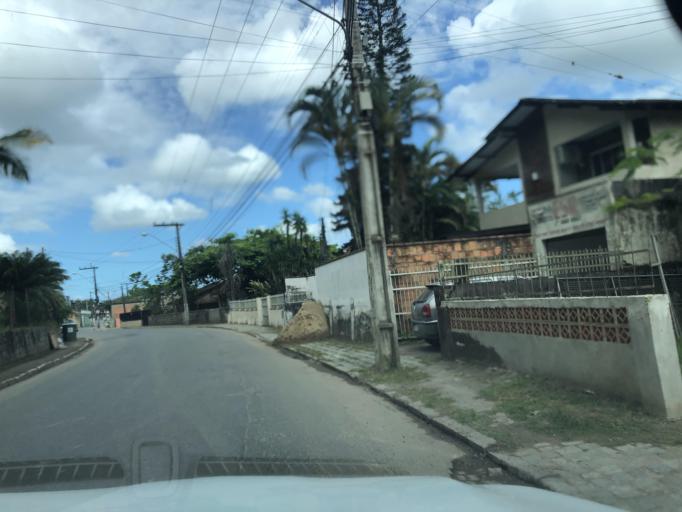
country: BR
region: Santa Catarina
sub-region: Sao Francisco Do Sul
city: Sao Francisco do Sul
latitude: -26.2441
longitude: -48.6332
